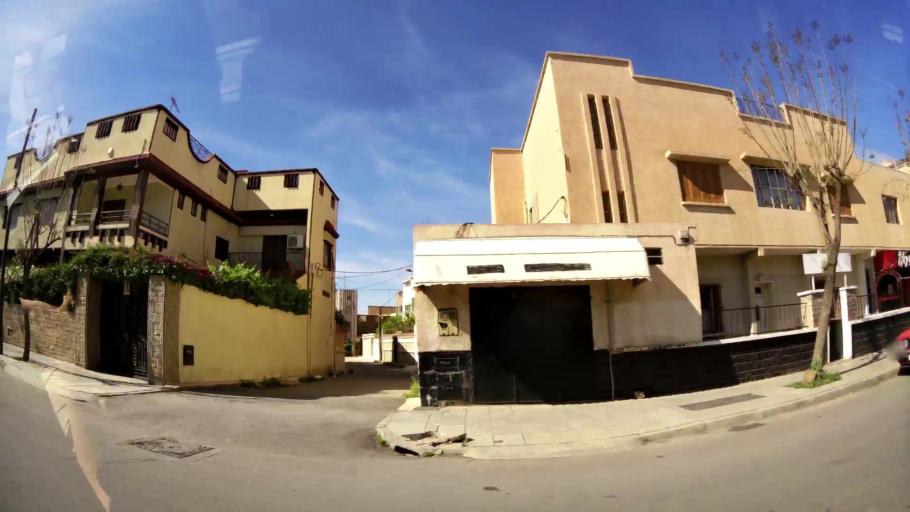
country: MA
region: Oriental
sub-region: Oujda-Angad
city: Oujda
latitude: 34.6721
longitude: -1.9096
